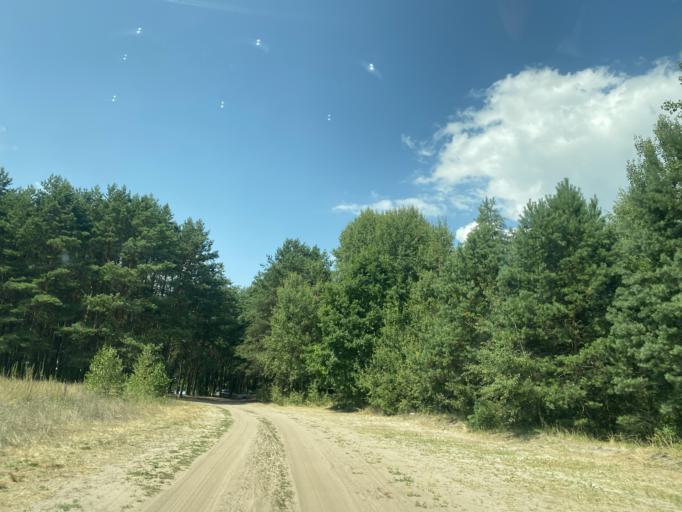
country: BY
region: Brest
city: Ivanava
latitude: 52.3663
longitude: 25.6336
